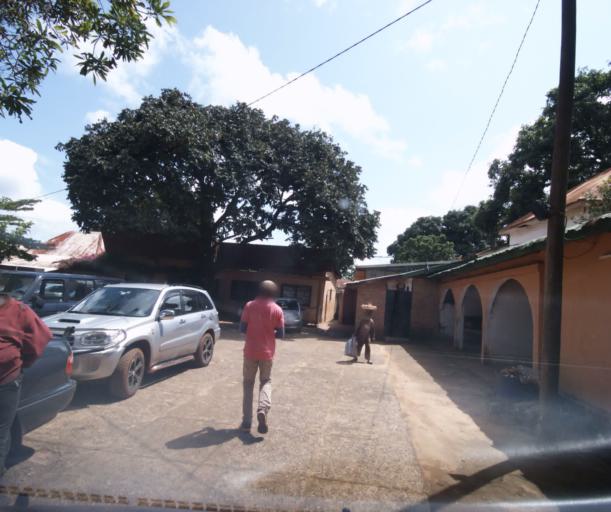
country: CM
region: West
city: Foumban
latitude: 5.7330
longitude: 10.9017
